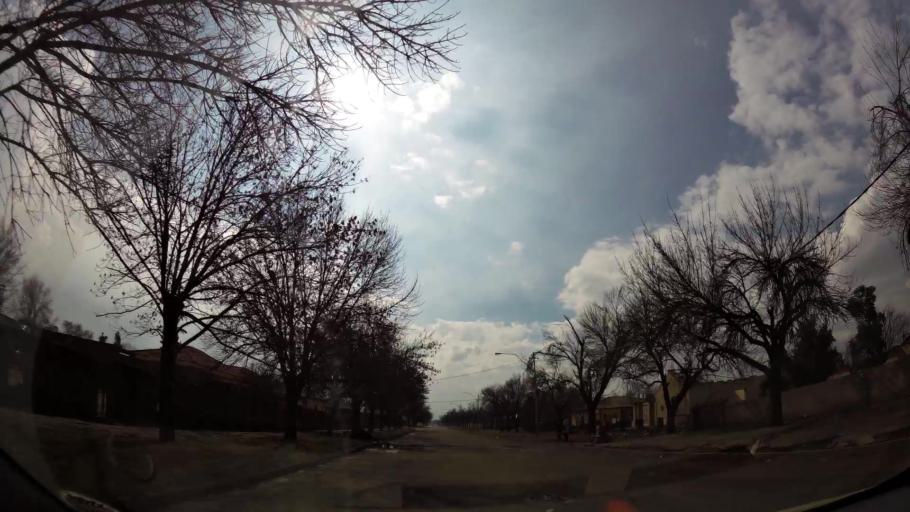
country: ZA
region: Gauteng
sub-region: Sedibeng District Municipality
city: Vereeniging
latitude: -26.6792
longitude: 27.9196
